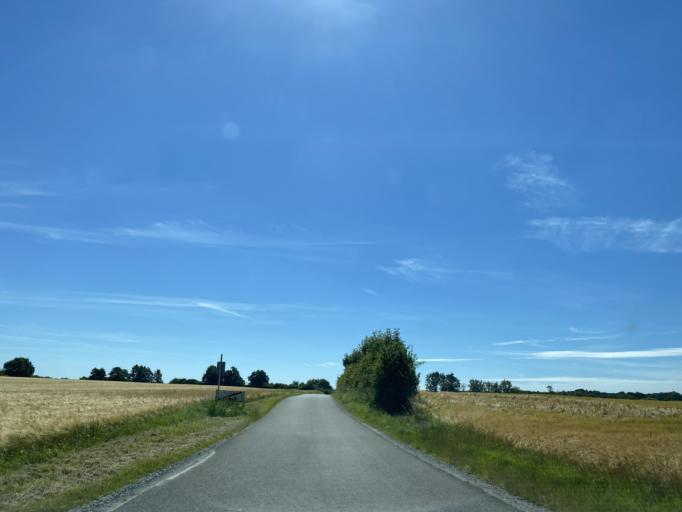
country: DK
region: South Denmark
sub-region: Vejle Kommune
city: Vejle
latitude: 55.6180
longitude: 9.5366
